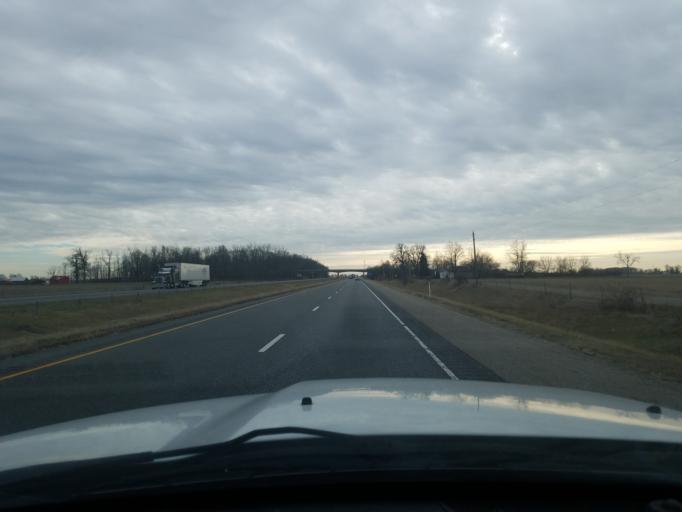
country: US
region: Indiana
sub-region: Grant County
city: Fairmount
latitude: 40.3682
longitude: -85.5591
